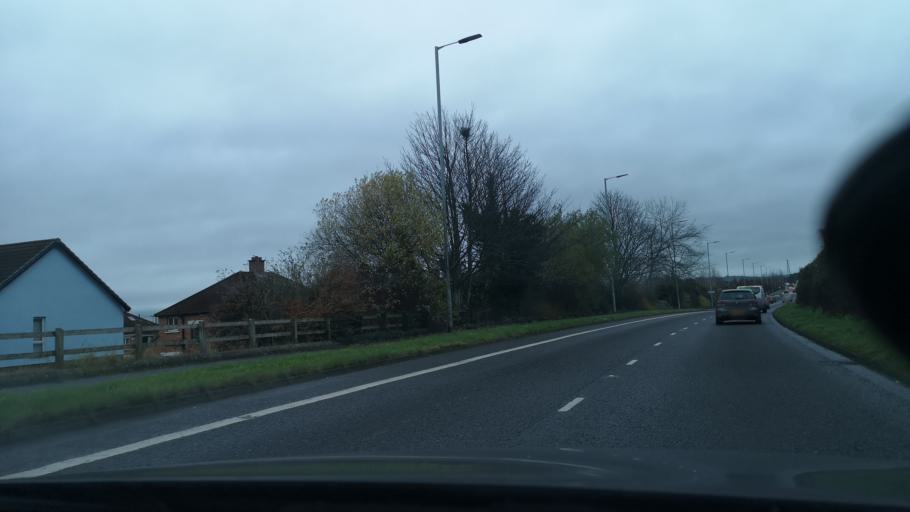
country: GB
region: Northern Ireland
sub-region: Castlereagh District
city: Castlereagh
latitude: 54.5740
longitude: -5.8824
